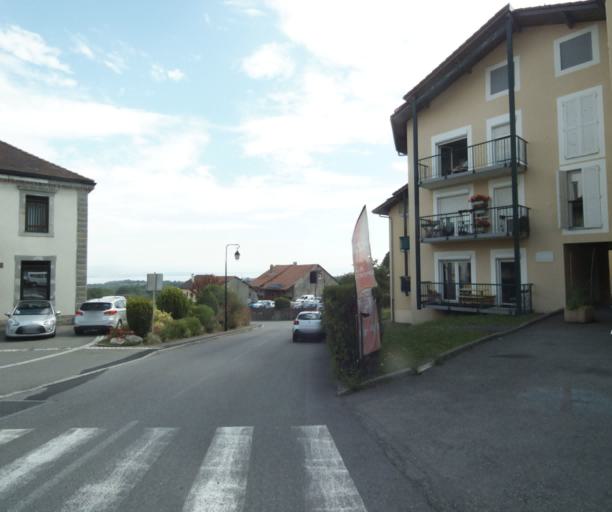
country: FR
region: Rhone-Alpes
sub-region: Departement de la Haute-Savoie
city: Allinges
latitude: 46.3362
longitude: 6.4642
